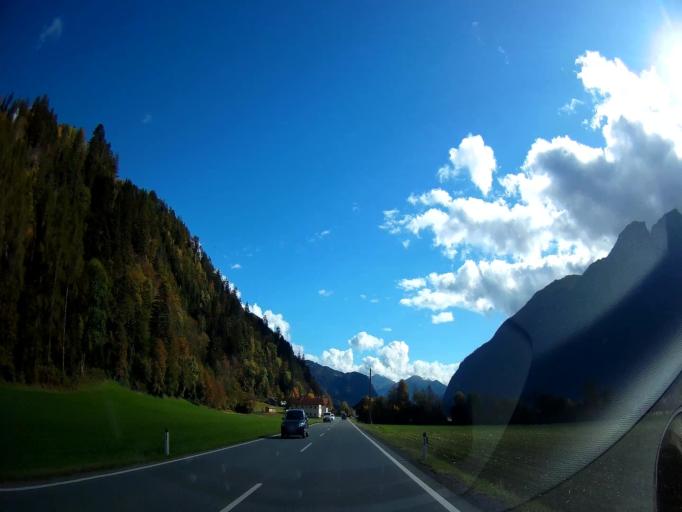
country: AT
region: Tyrol
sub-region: Politischer Bezirk Lienz
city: Lavant
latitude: 46.8098
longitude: 12.8520
